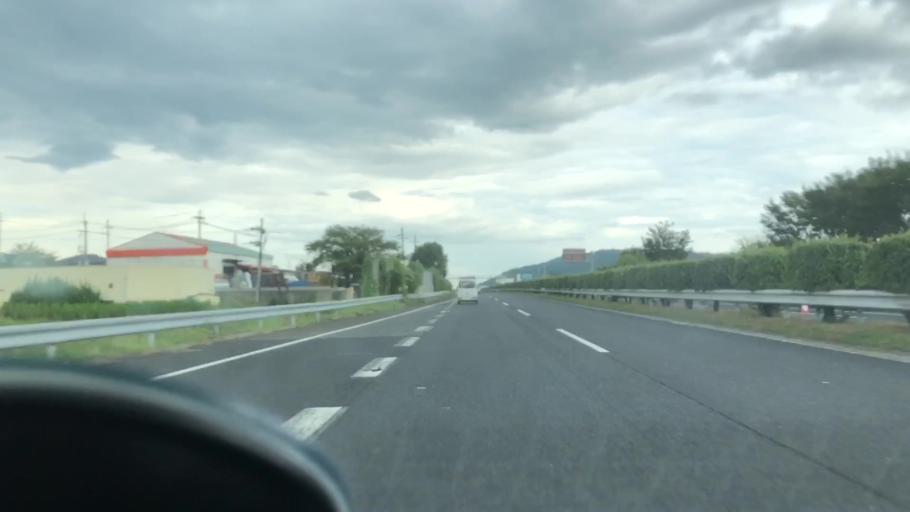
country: JP
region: Hyogo
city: Himeji
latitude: 34.9481
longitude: 134.7673
